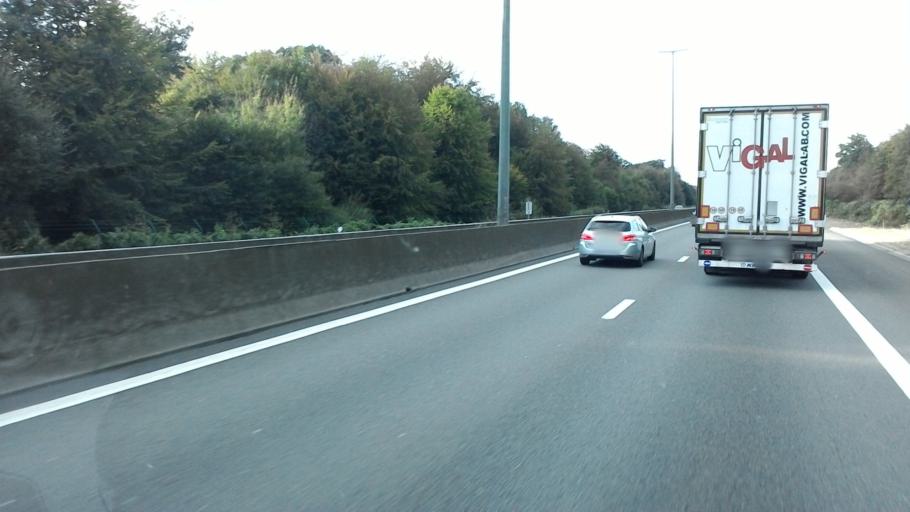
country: BE
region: Wallonia
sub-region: Province du Luxembourg
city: Habay-la-Vieille
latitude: 49.7412
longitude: 5.5737
